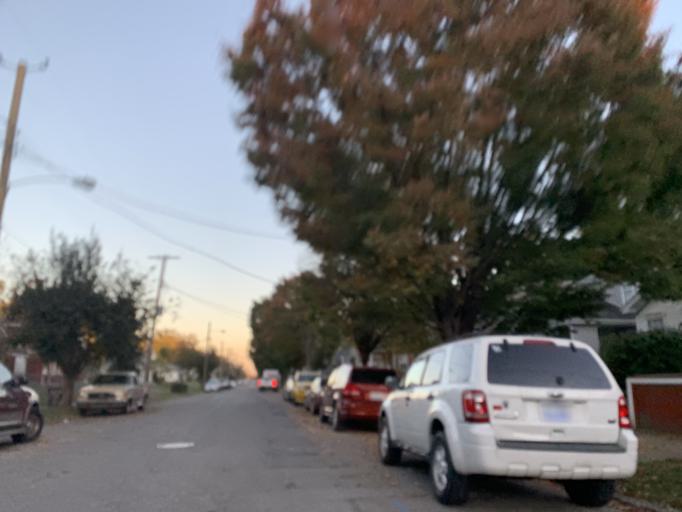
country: US
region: Kentucky
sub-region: Jefferson County
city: Louisville
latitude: 38.2351
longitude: -85.7856
